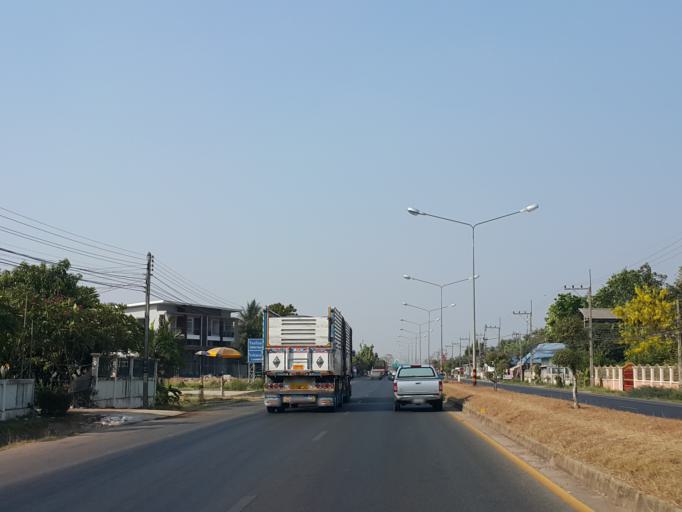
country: TH
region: Phitsanulok
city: Phitsanulok
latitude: 16.8387
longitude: 100.3396
